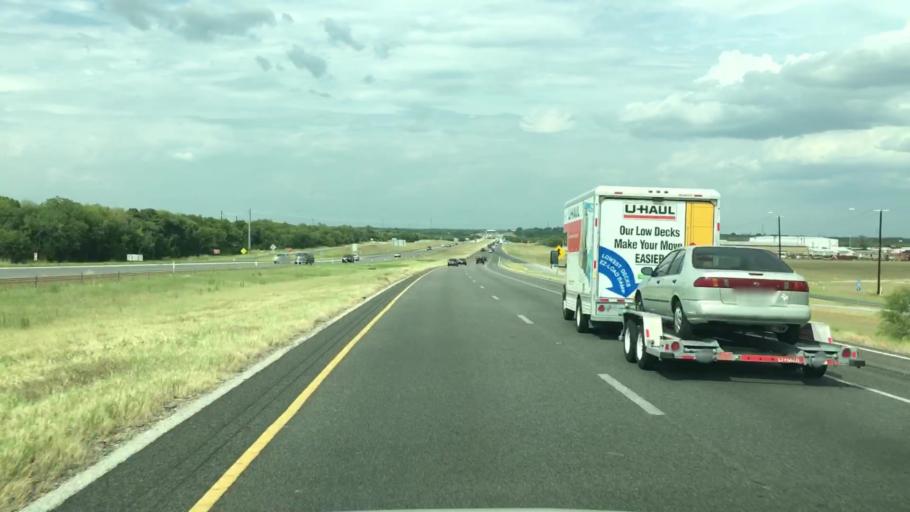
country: US
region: Texas
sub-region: Bexar County
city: Elmendorf
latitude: 29.2198
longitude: -98.4117
